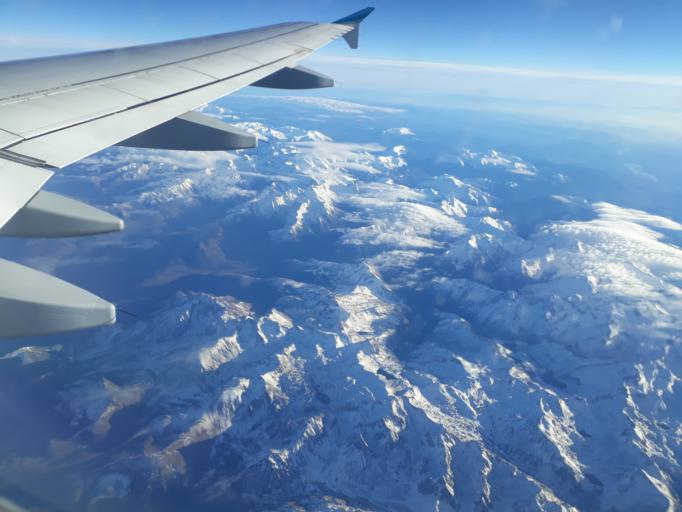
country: FR
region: Midi-Pyrenees
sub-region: Departement des Hautes-Pyrenees
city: Campan
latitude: 42.9860
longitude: 0.1122
